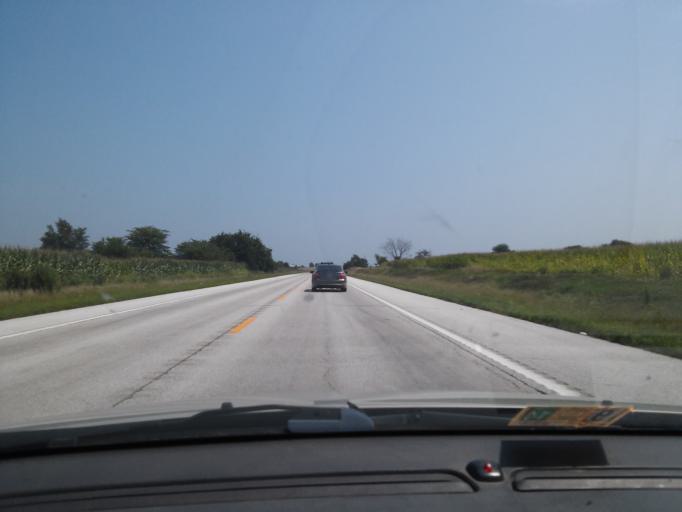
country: US
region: Missouri
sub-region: Pike County
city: Bowling Green
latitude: 39.3505
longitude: -91.2225
